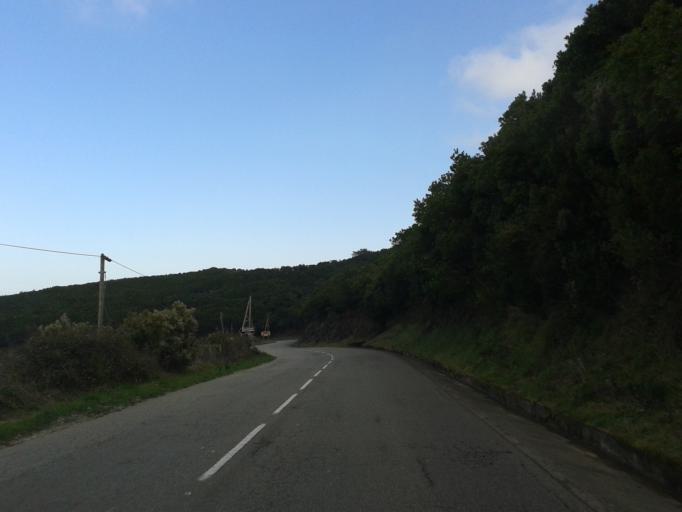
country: FR
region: Corsica
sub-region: Departement de la Haute-Corse
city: Biguglia
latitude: 42.5984
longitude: 9.4058
